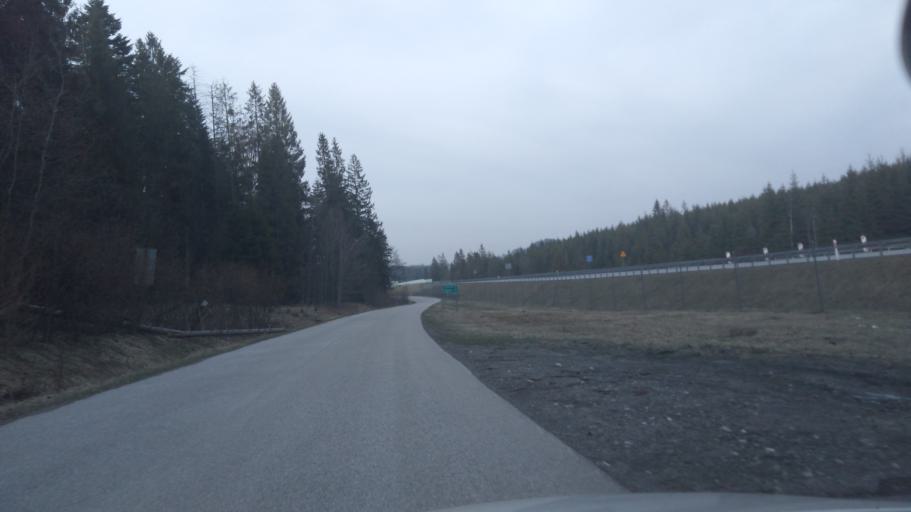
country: PL
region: Silesian Voivodeship
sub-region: Powiat zywiecki
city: Laliki
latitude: 49.5147
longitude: 18.9809
